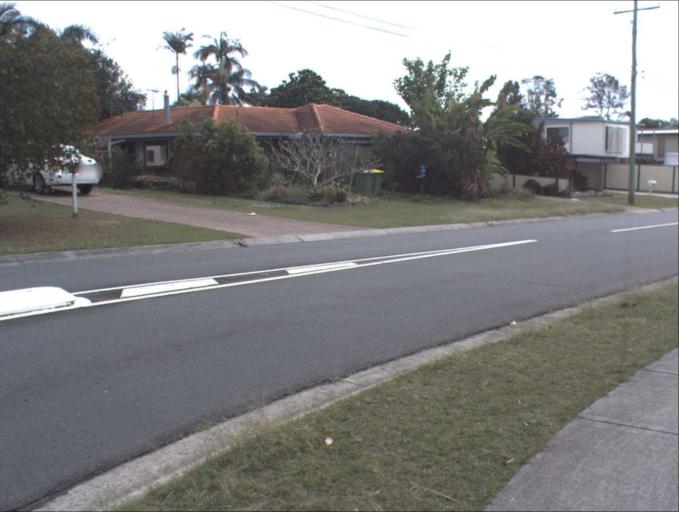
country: AU
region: Queensland
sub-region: Logan
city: Logan Reserve
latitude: -27.6845
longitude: 153.0862
